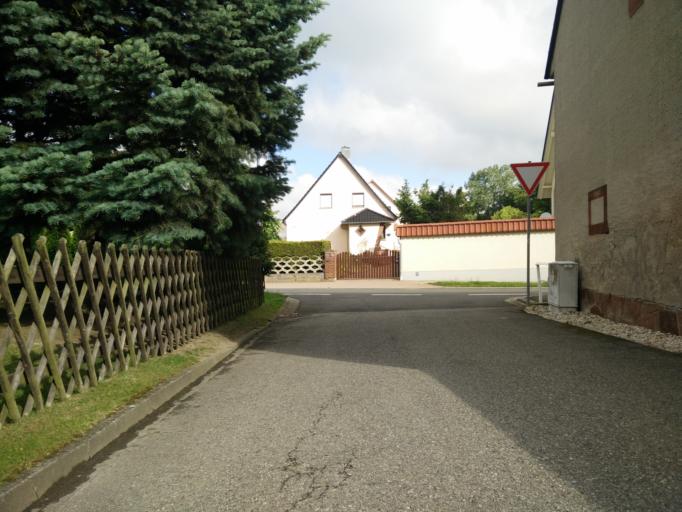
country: DE
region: Saxony
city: Geithain
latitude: 51.0503
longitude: 12.6961
